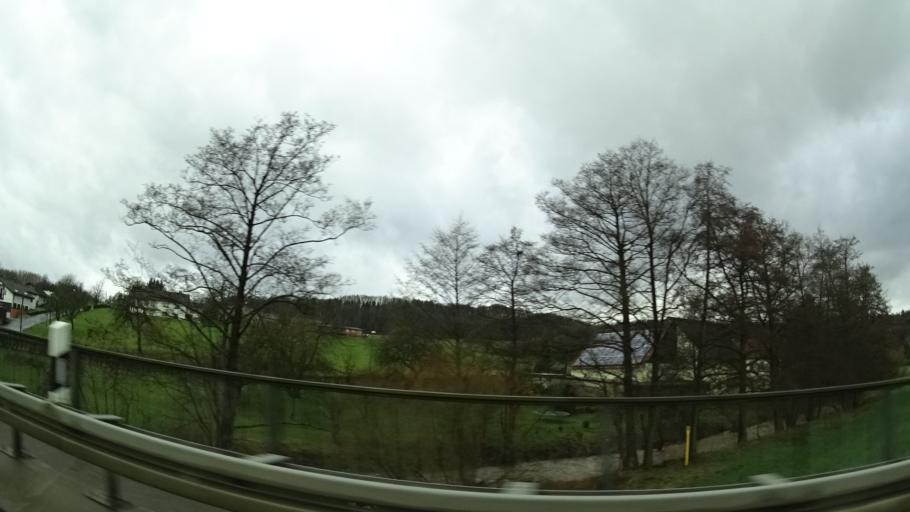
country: DE
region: Hesse
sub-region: Regierungsbezirk Darmstadt
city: Schluchtern
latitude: 50.3305
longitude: 9.4996
